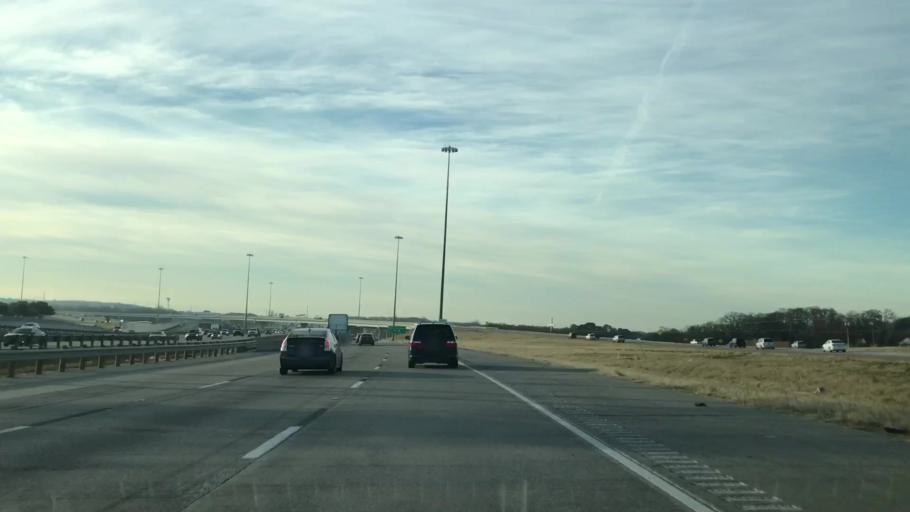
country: US
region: Texas
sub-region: Tarrant County
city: Grapevine
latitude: 32.9146
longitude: -97.0971
